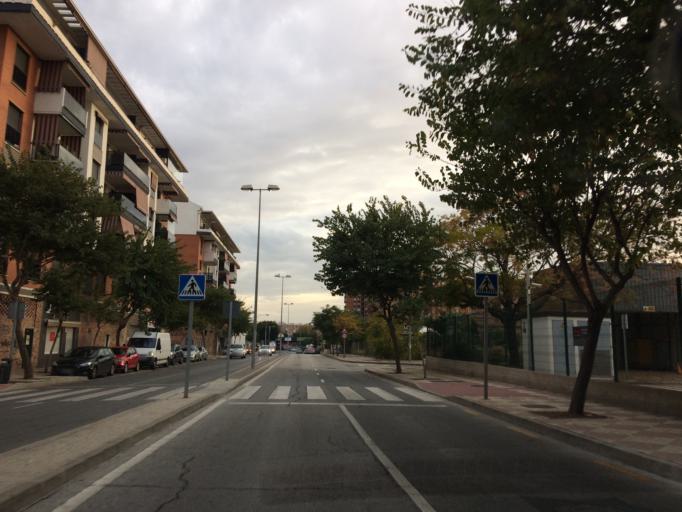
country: ES
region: Andalusia
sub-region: Provincia de Malaga
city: Malaga
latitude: 36.7078
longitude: -4.4551
